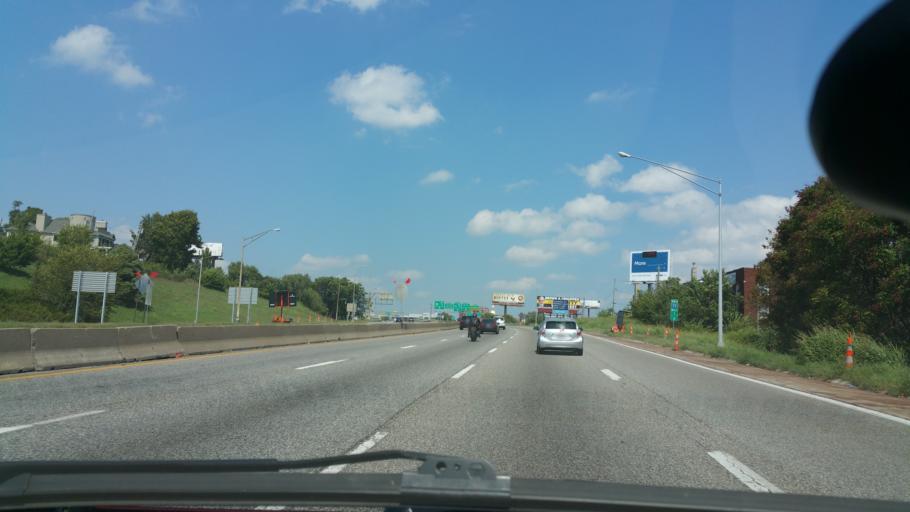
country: US
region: Missouri
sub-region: Jackson County
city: Kansas City
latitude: 39.0901
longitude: -94.5912
